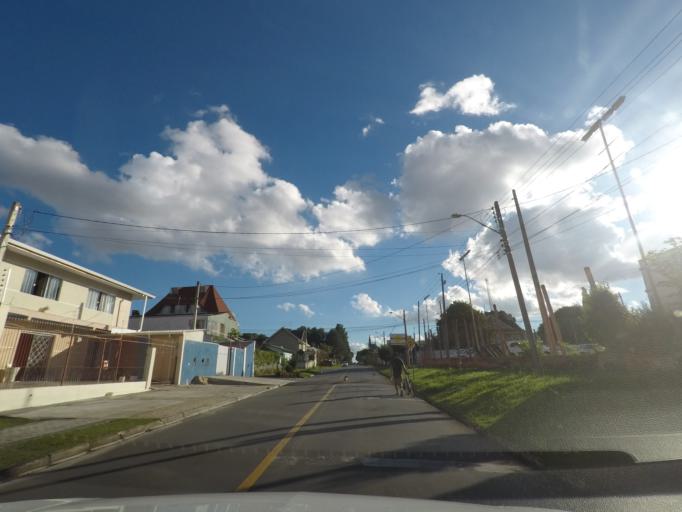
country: BR
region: Parana
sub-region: Curitiba
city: Curitiba
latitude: -25.4812
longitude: -49.2579
